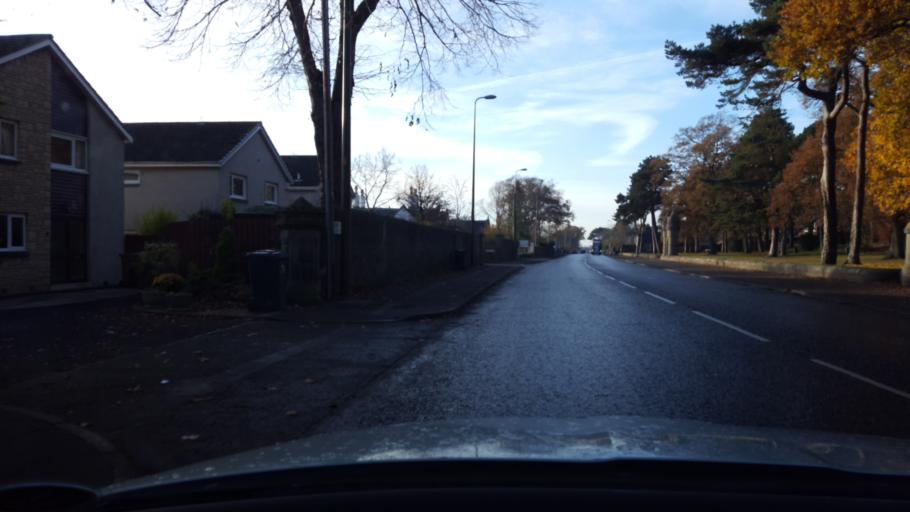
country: GB
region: Scotland
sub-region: Fife
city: Tayport
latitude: 56.4704
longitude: -2.8539
